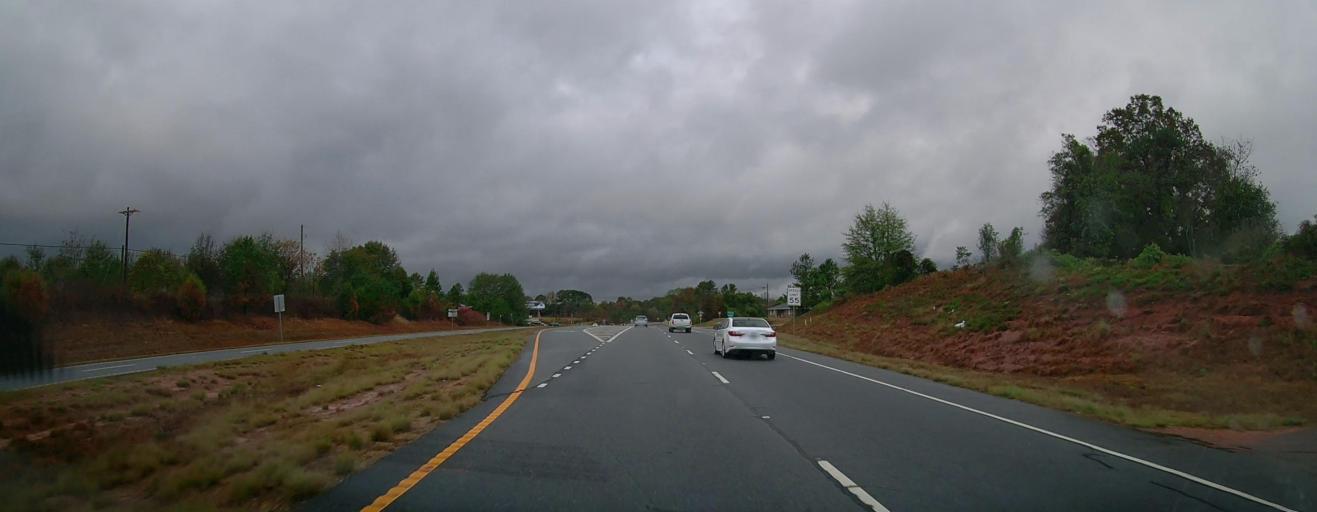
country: US
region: Georgia
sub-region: Jackson County
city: Nicholson
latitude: 34.0959
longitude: -83.4303
